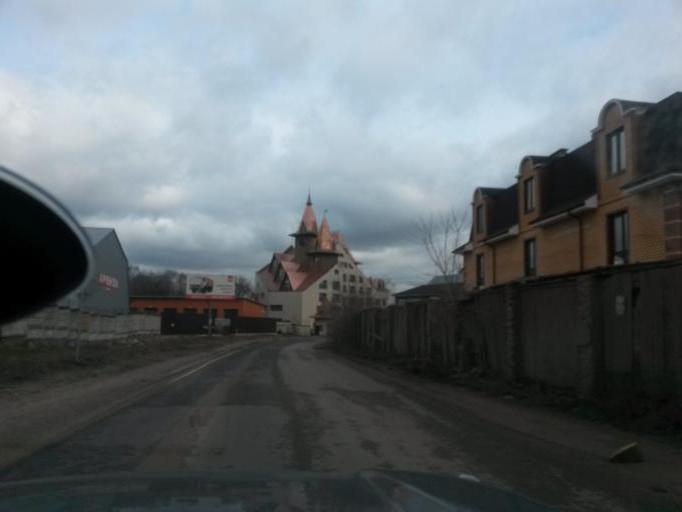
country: RU
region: Moscow
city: Zyablikovo
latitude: 55.6103
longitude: 37.7850
